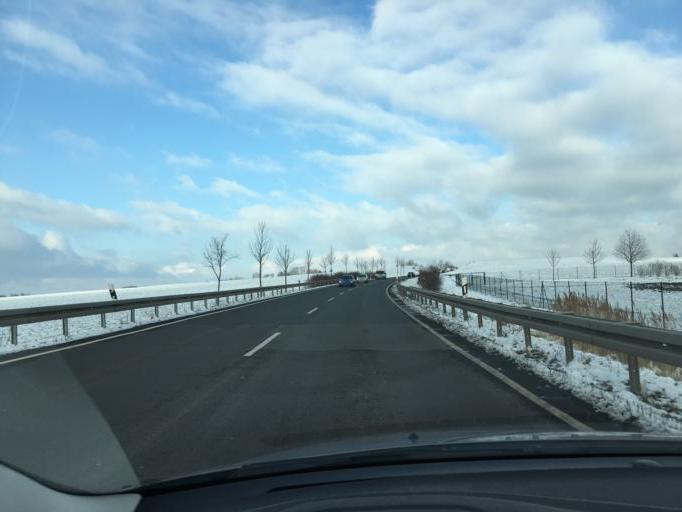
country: DE
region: Saxony
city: Grimma
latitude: 51.2411
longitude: 12.6995
